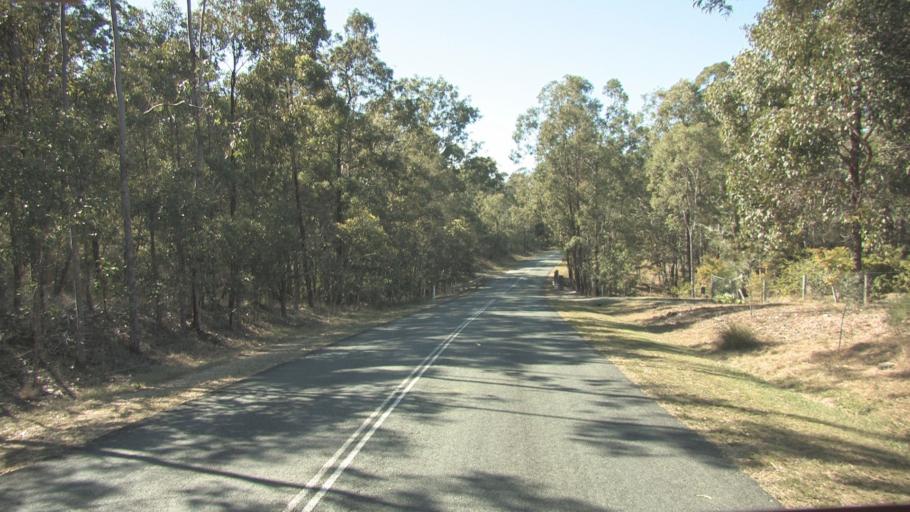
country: AU
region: Queensland
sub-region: Ipswich
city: Springfield Lakes
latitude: -27.7103
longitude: 152.9243
